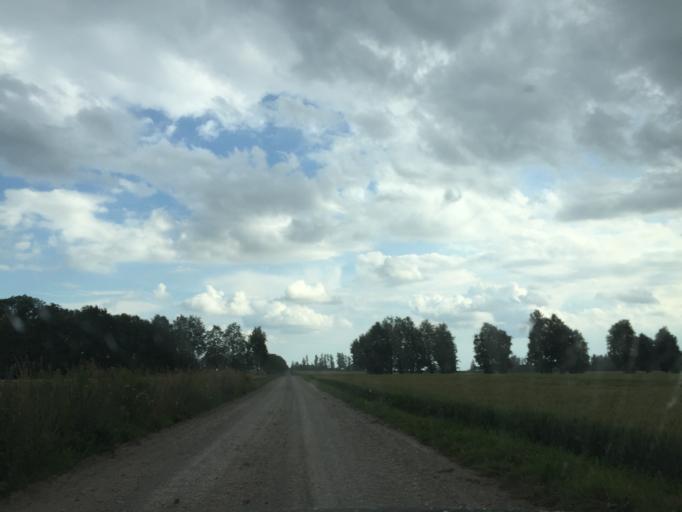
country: LV
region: Dobeles Rajons
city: Dobele
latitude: 56.6254
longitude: 23.3963
